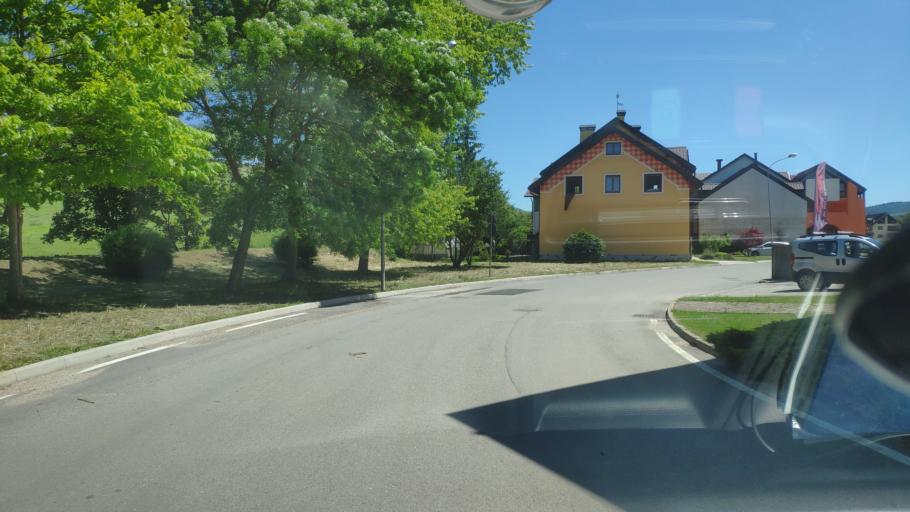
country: IT
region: Veneto
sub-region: Provincia di Vicenza
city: Canove di Roana
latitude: 45.8594
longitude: 11.4846
